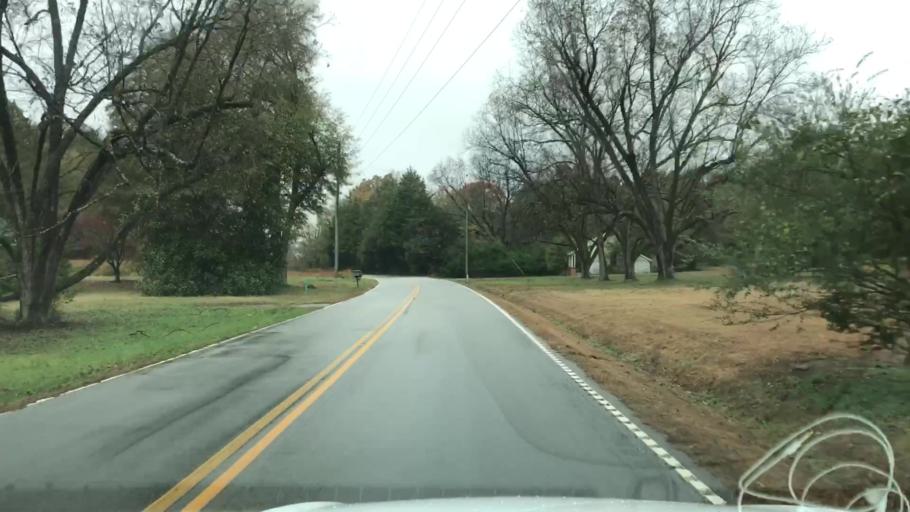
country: US
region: South Carolina
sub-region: Spartanburg County
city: Roebuck
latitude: 34.7805
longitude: -81.9124
